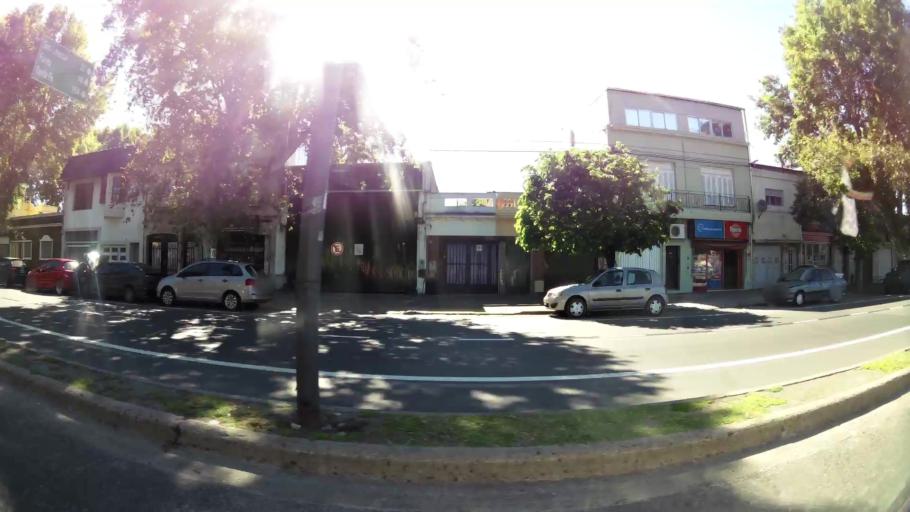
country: AR
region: Santa Fe
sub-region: Departamento de Rosario
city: Rosario
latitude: -32.9494
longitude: -60.6817
